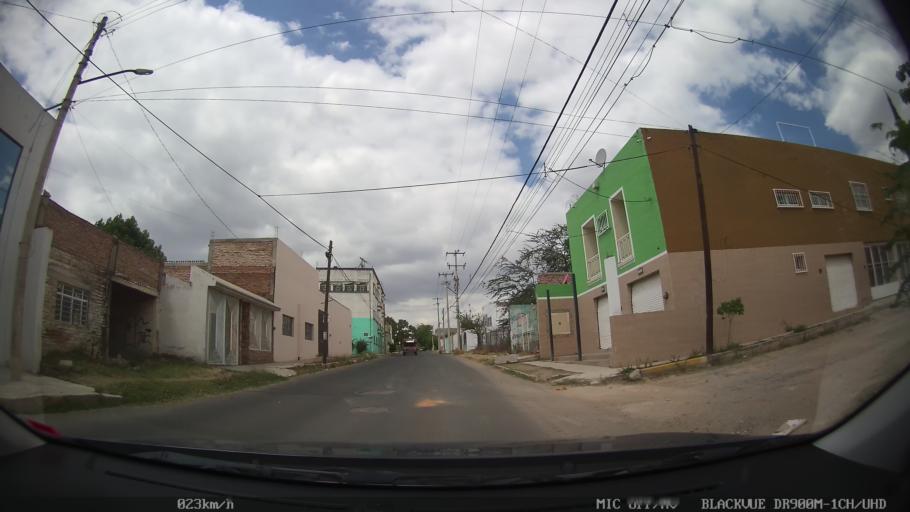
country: MX
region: Jalisco
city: Tlaquepaque
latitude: 20.6398
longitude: -103.2628
